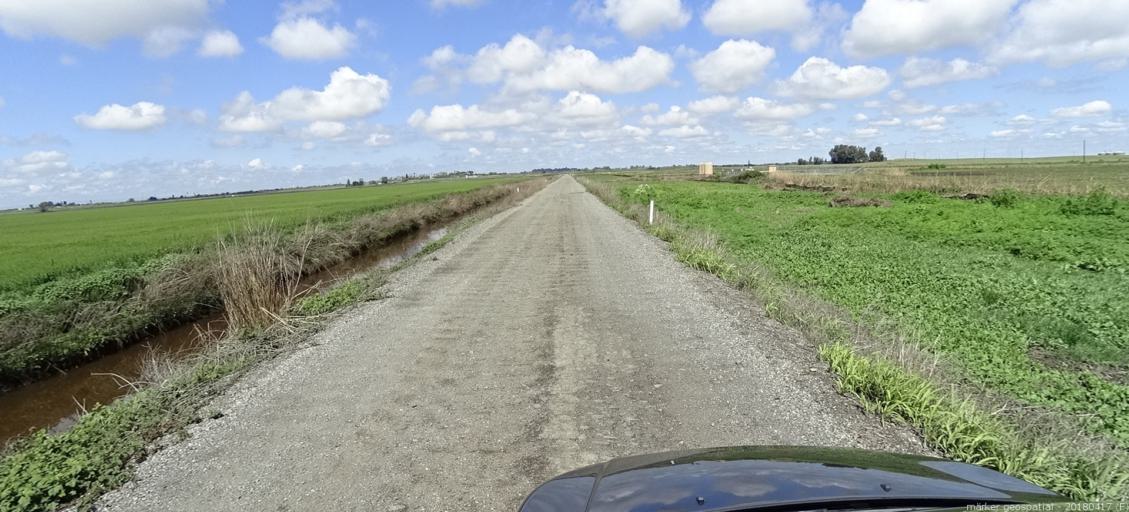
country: US
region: California
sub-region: Solano County
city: Rio Vista
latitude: 38.1334
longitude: -121.5801
